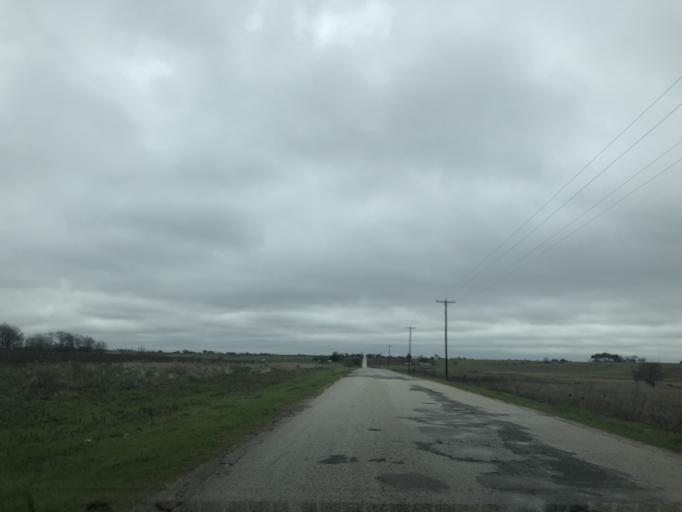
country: US
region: Texas
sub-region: Williamson County
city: Hutto
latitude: 30.5914
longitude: -97.5006
